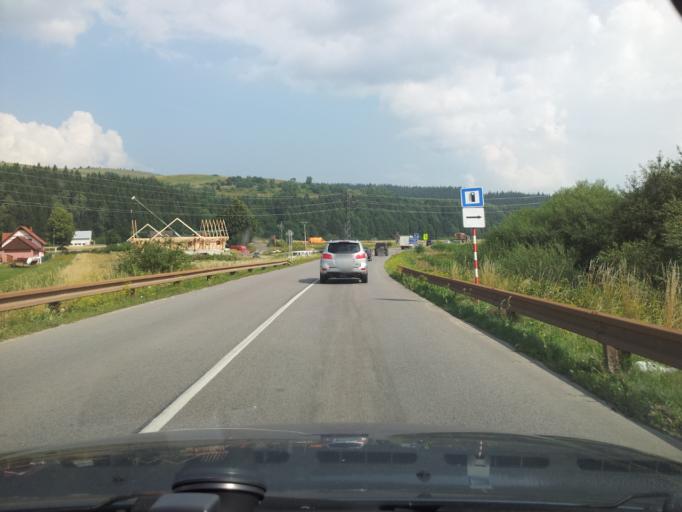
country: SK
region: Zilinsky
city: Namestovo
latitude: 49.3896
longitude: 19.4514
